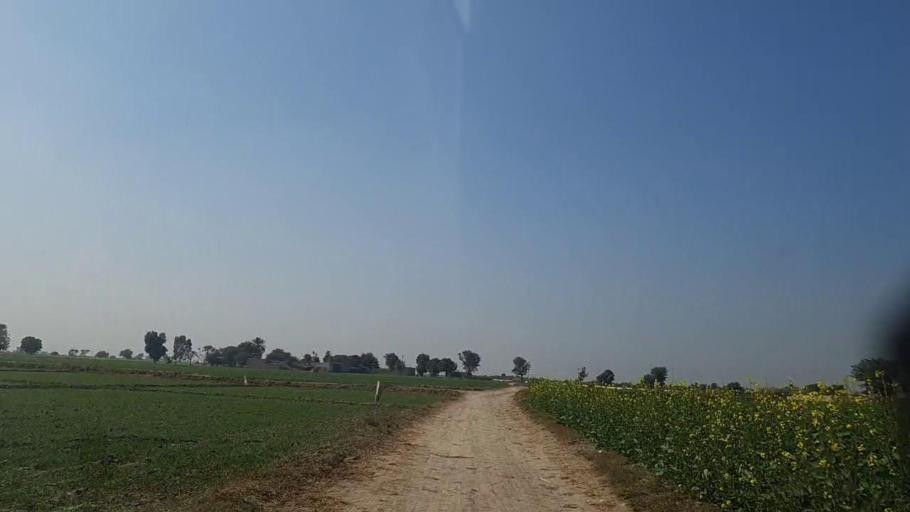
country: PK
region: Sindh
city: Sakrand
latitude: 26.1625
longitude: 68.3236
